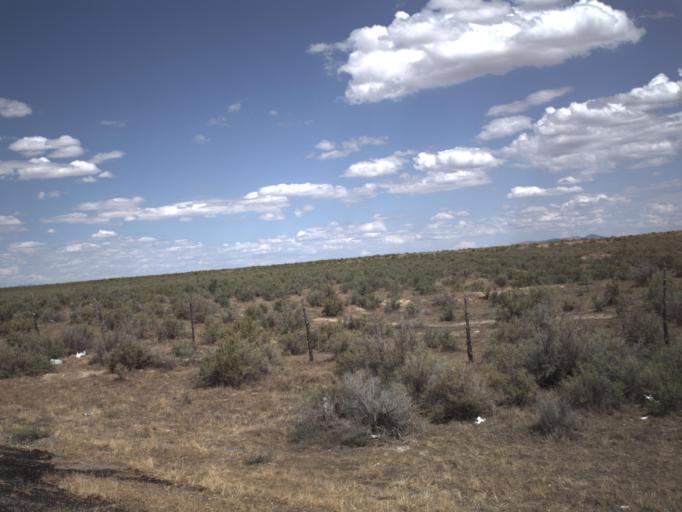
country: US
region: Utah
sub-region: Millard County
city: Delta
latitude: 39.3413
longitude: -112.4925
